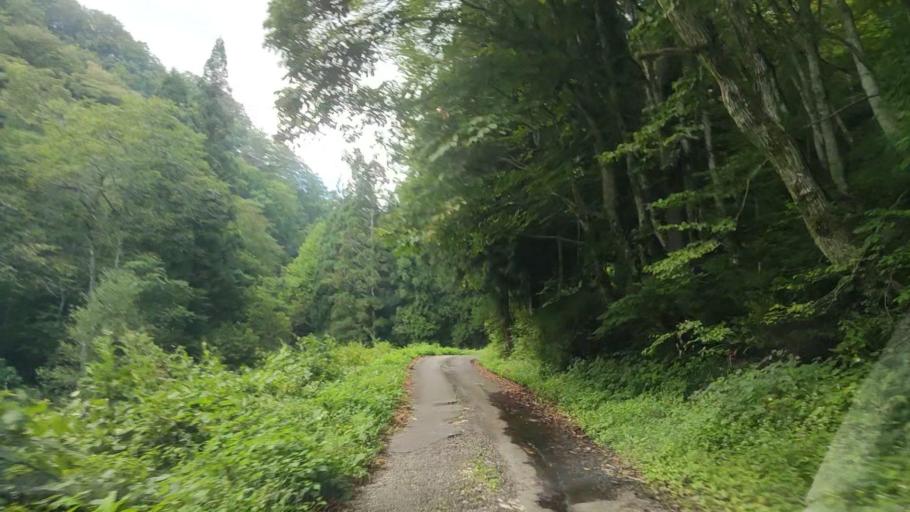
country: JP
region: Gifu
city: Takayama
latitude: 36.3171
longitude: 137.0841
